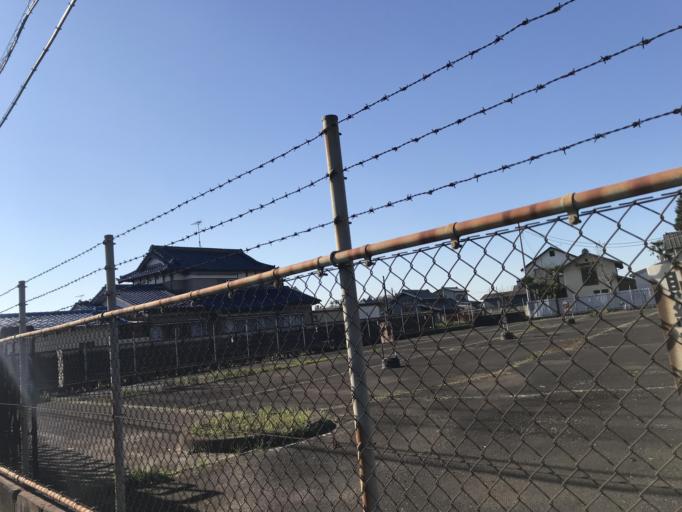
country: JP
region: Ibaraki
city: Sakai
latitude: 36.1450
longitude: 139.8115
